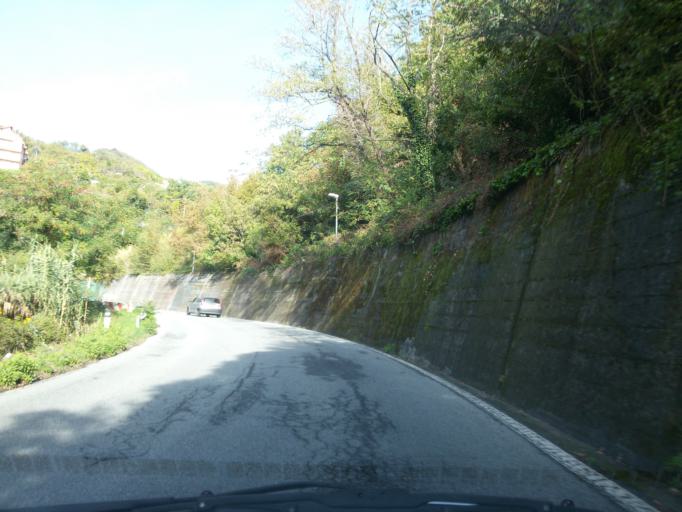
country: IT
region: Liguria
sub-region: Provincia di Genova
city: Piccarello
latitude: 44.4856
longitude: 8.9744
